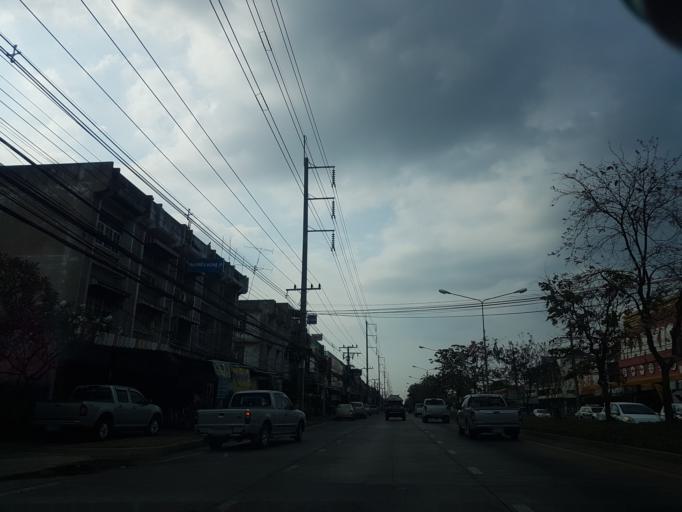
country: TH
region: Sara Buri
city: Phra Phutthabat
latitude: 14.7295
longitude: 100.7883
